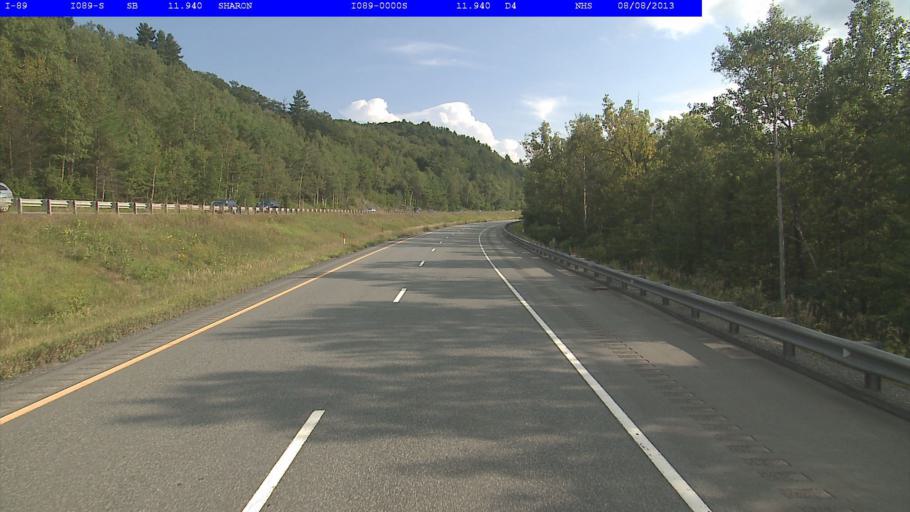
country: US
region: Vermont
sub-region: Windsor County
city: Woodstock
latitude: 43.7672
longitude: -72.4457
